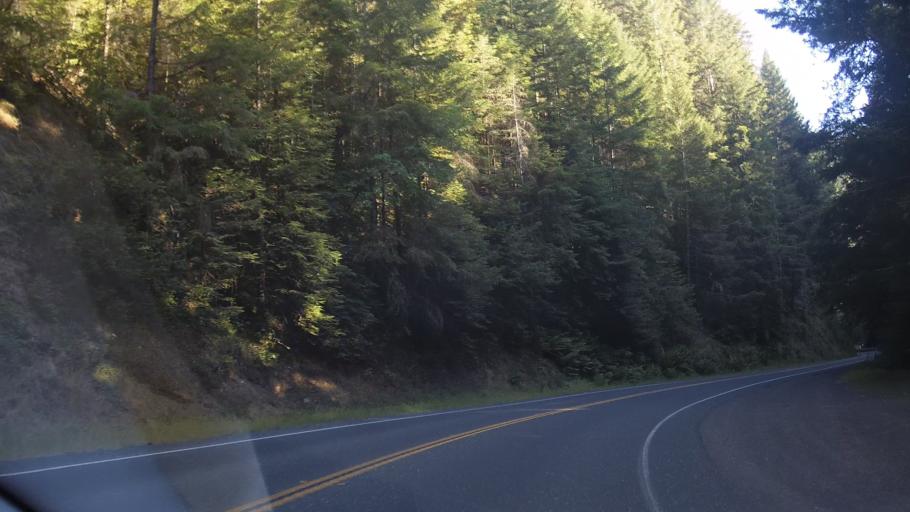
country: US
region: California
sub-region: Mendocino County
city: Brooktrails
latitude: 39.3506
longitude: -123.5107
